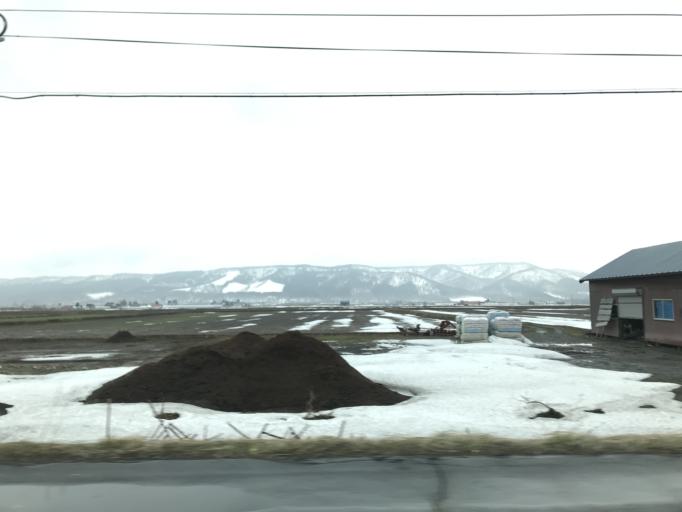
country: JP
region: Hokkaido
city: Nayoro
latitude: 44.2338
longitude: 142.3947
